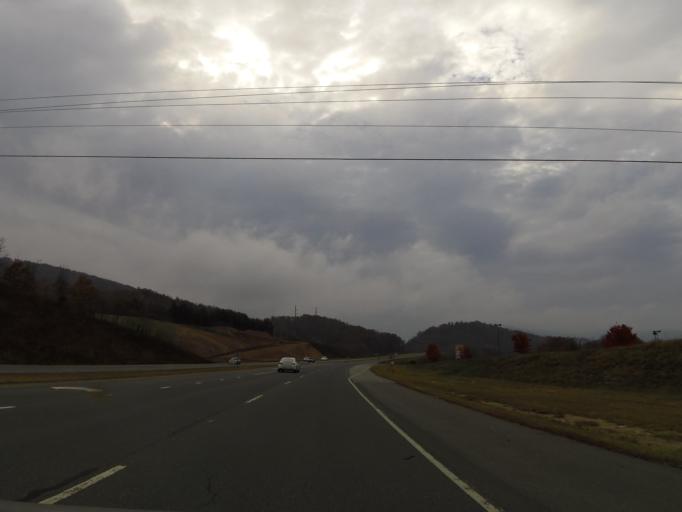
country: US
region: North Carolina
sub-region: Watauga County
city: Boone
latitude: 36.2255
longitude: -81.6100
